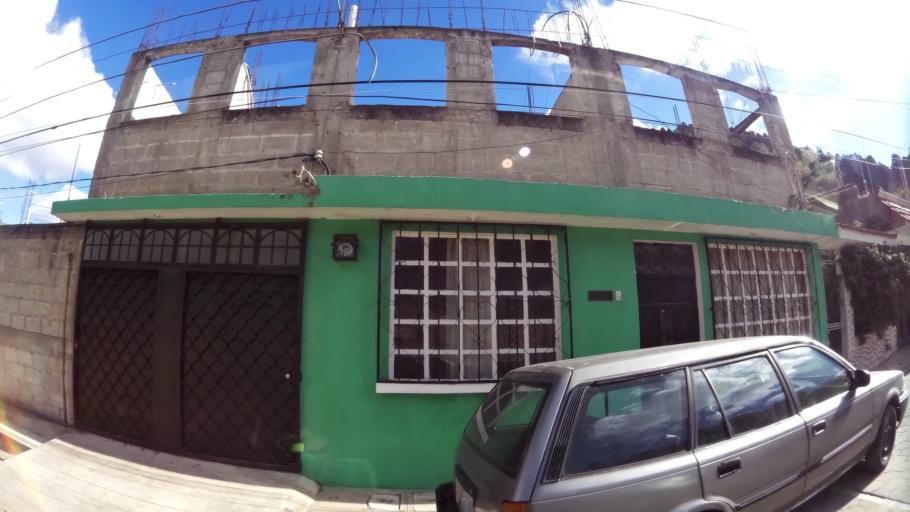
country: GT
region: Quetzaltenango
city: Quetzaltenango
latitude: 14.8288
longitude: -91.5083
